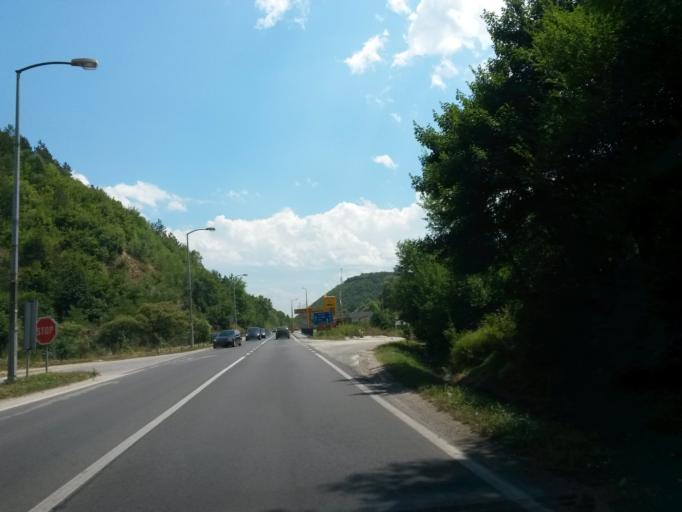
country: BA
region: Federation of Bosnia and Herzegovina
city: Travnik
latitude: 44.2280
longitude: 17.6797
